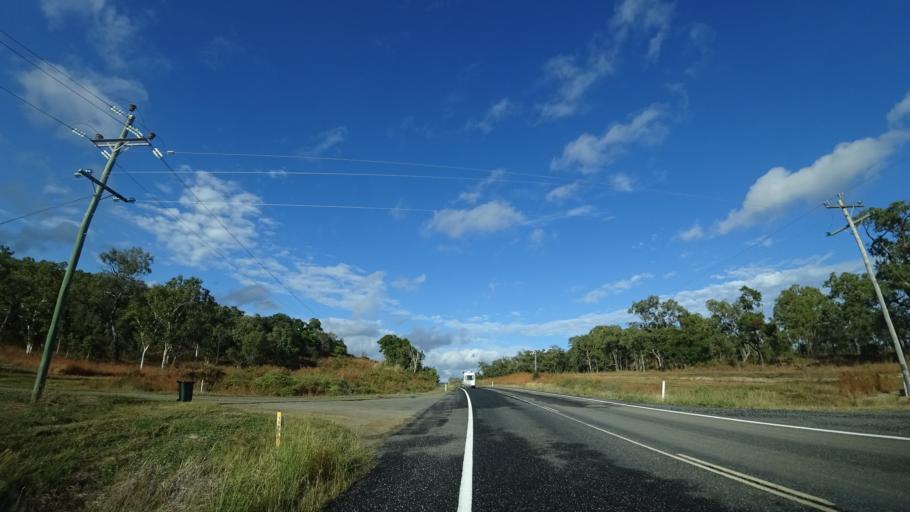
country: AU
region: Queensland
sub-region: Cook
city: Cooktown
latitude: -15.6032
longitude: 145.2233
